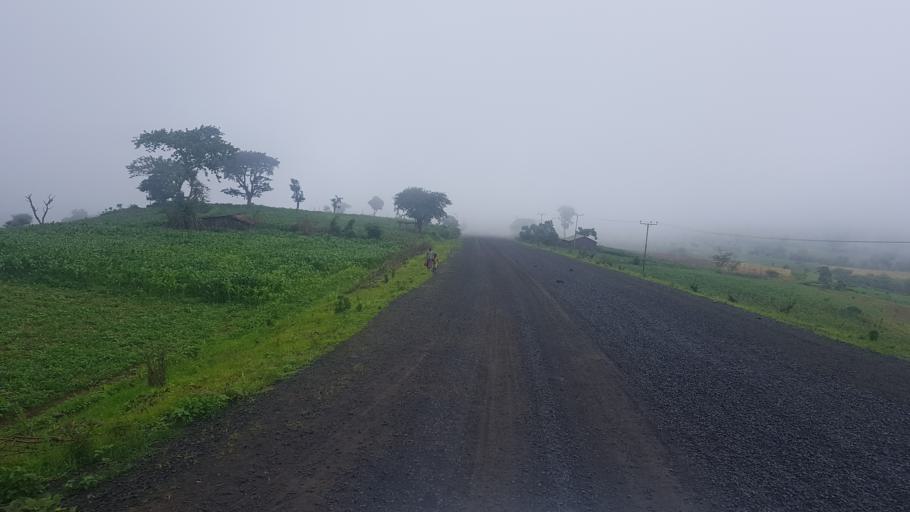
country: ET
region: Amhara
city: Bure
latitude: 10.1961
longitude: 36.9757
